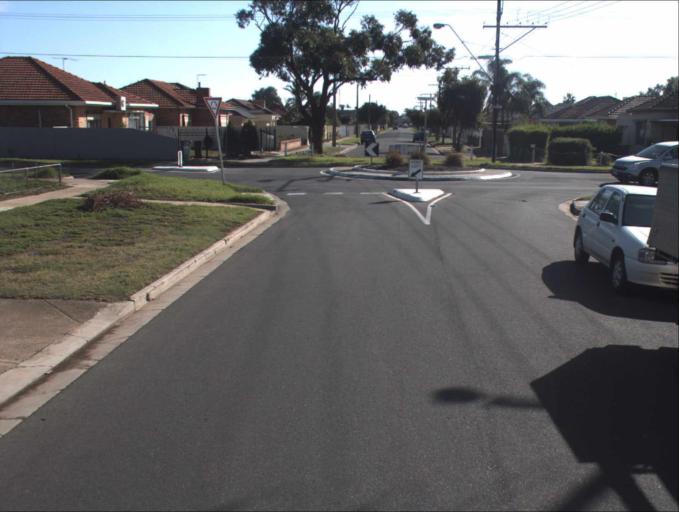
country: AU
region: South Australia
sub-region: Charles Sturt
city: Woodville North
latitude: -34.8545
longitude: 138.5492
